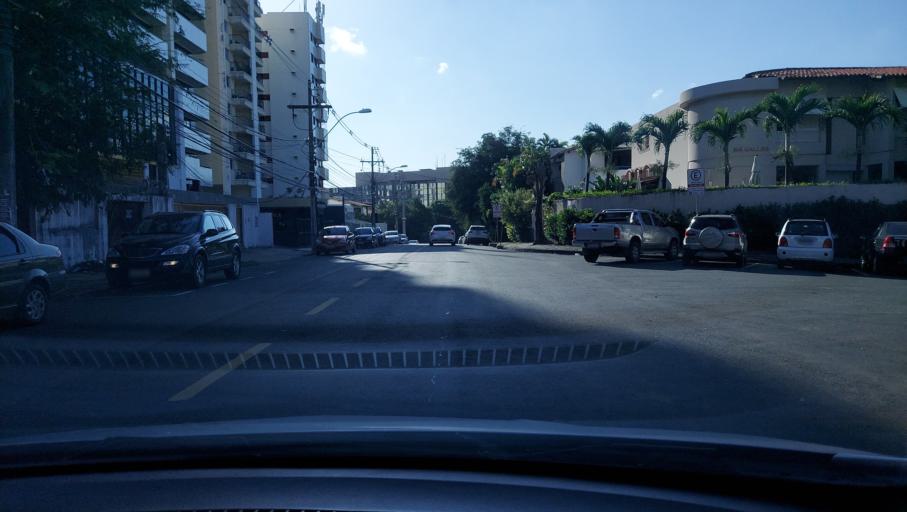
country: BR
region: Bahia
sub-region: Salvador
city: Salvador
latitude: -12.9811
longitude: -38.4609
